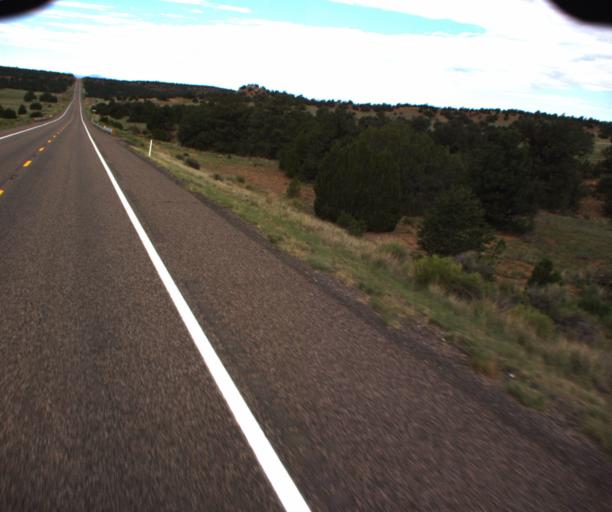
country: US
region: Arizona
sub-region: Apache County
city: Springerville
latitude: 34.1632
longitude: -109.0656
